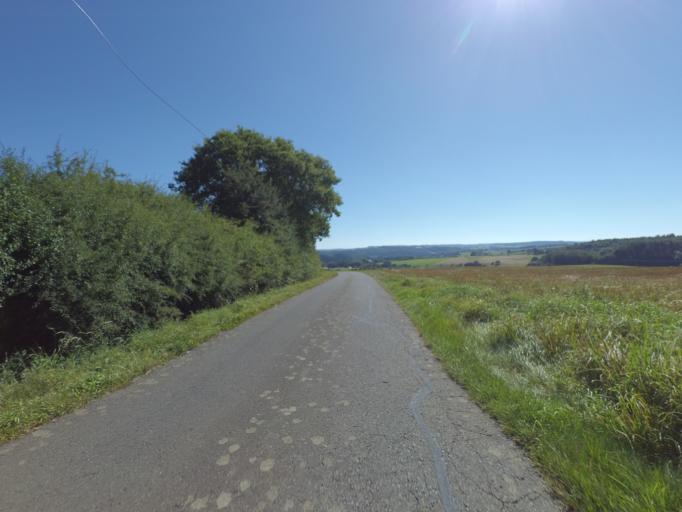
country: DE
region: Rheinland-Pfalz
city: Utzerath
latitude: 50.2209
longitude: 6.9229
